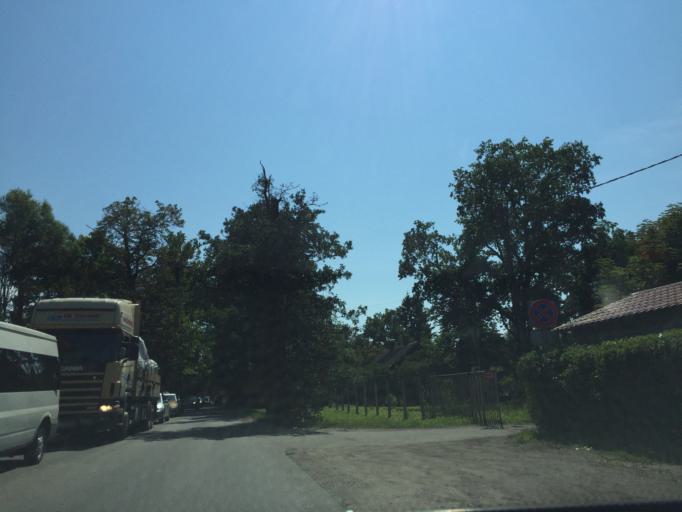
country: LV
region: Marupe
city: Marupe
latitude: 56.9524
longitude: 23.9977
